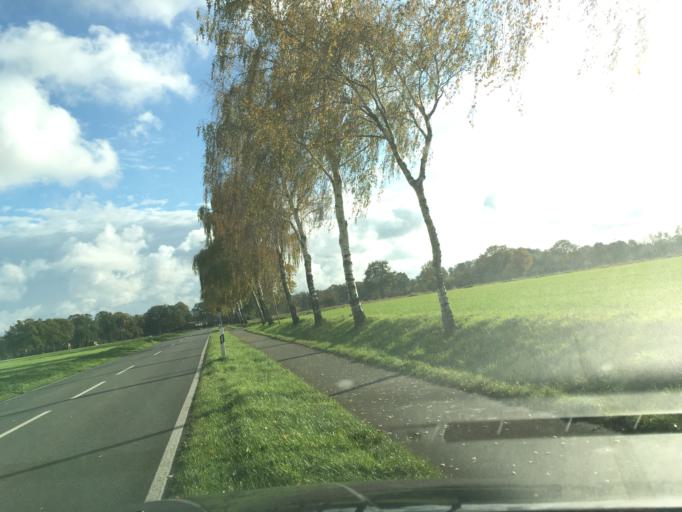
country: DE
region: North Rhine-Westphalia
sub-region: Regierungsbezirk Munster
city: Vreden
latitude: 52.0978
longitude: 6.8629
